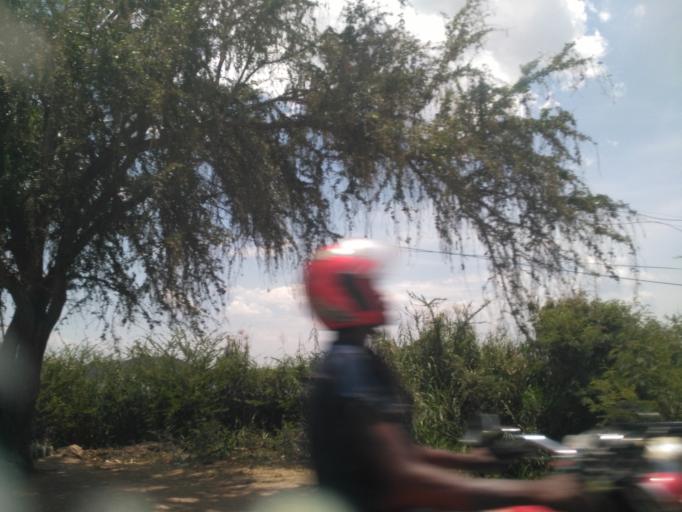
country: TZ
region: Mwanza
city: Mwanza
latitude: -2.5529
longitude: 32.9077
